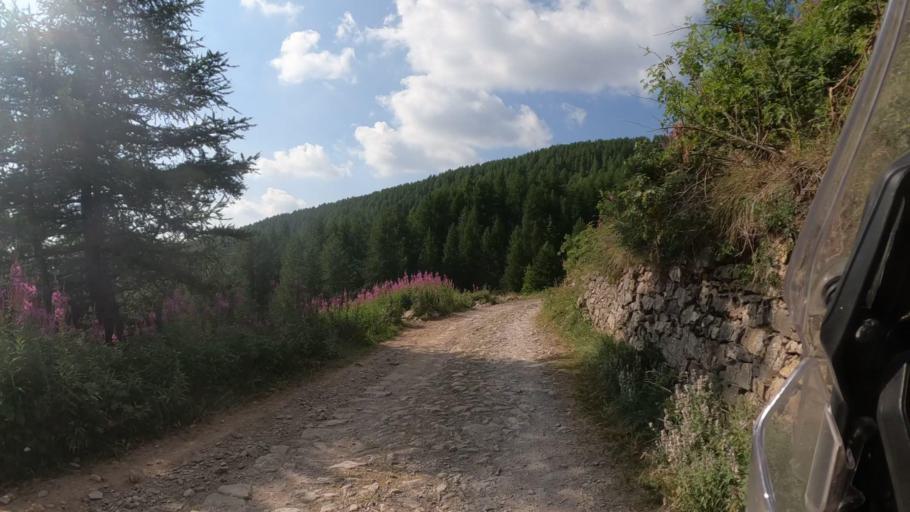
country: IT
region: Piedmont
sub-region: Provincia di Cuneo
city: Briga Alta
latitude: 44.1231
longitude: 7.6905
